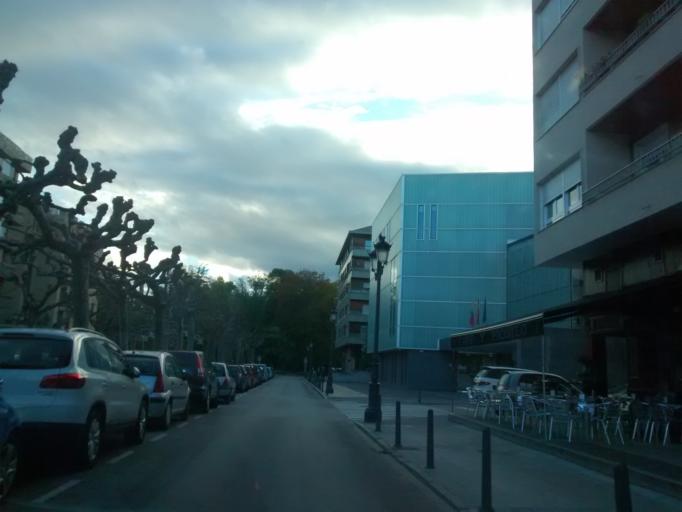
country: ES
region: Cantabria
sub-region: Provincia de Cantabria
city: Torrelavega
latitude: 43.3469
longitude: -4.0517
